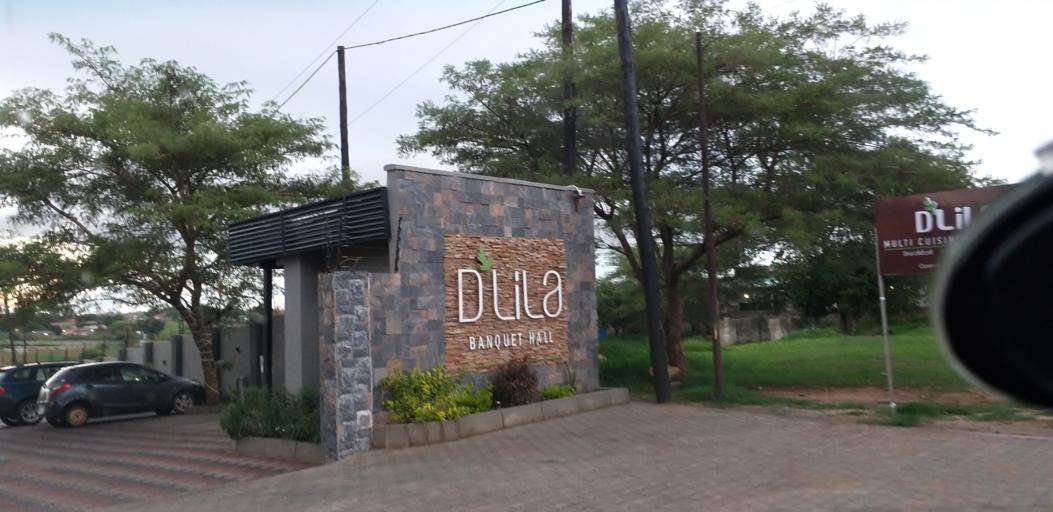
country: ZM
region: Lusaka
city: Lusaka
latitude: -15.4151
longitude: 28.3689
